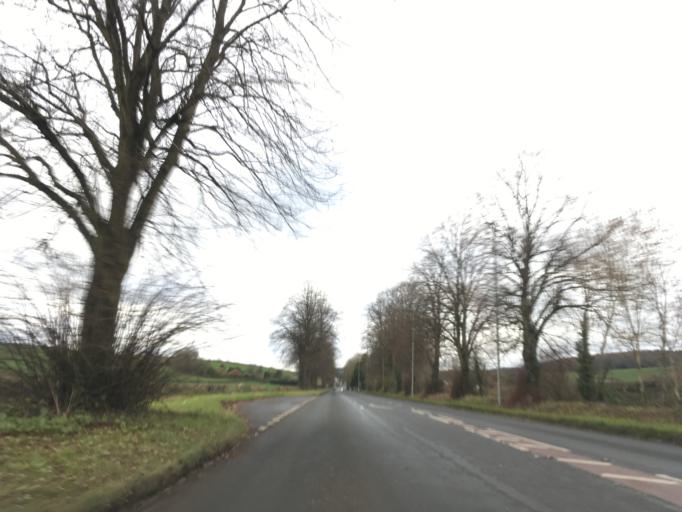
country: GB
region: Wales
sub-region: Newport
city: Llanvaches
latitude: 51.6151
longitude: -2.8361
